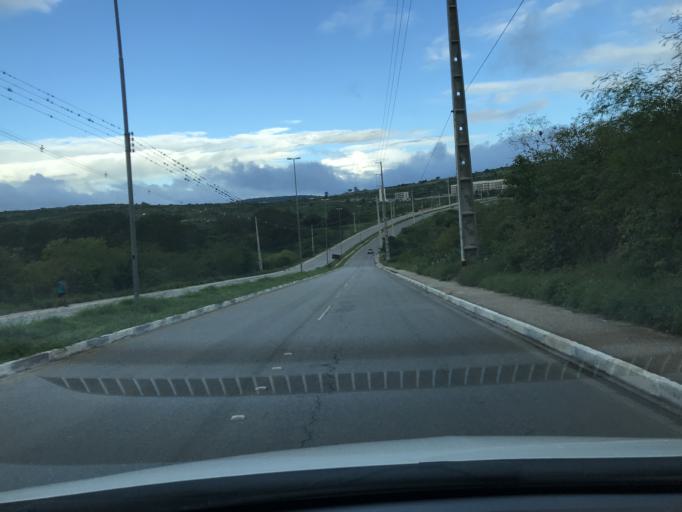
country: BR
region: Pernambuco
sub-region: Caruaru
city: Caruaru
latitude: -8.2966
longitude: -35.9407
